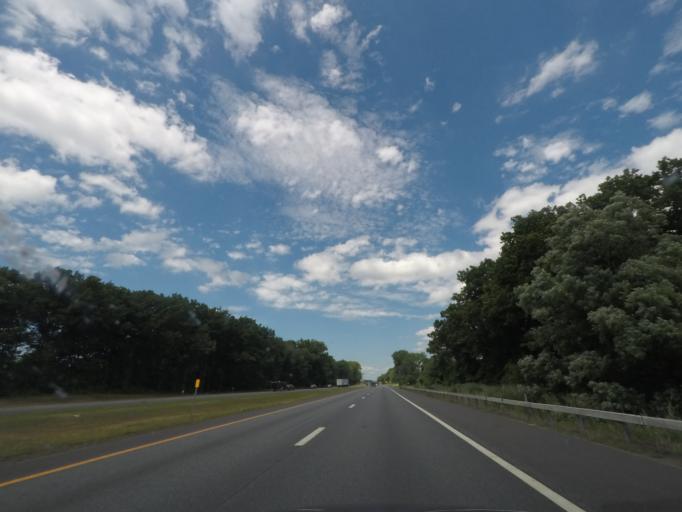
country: US
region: New York
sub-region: Albany County
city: Westmere
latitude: 42.7060
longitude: -73.8542
